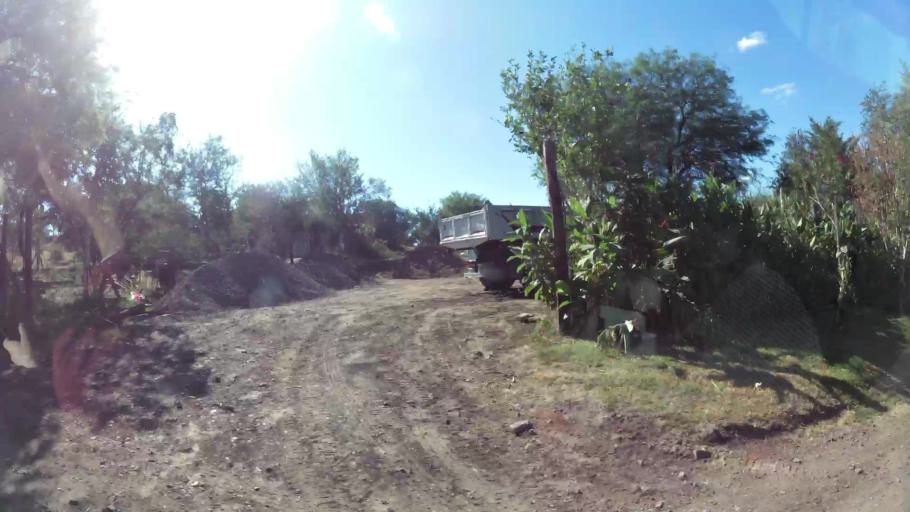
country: AR
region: Cordoba
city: La Calera
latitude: -31.3527
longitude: -64.3143
